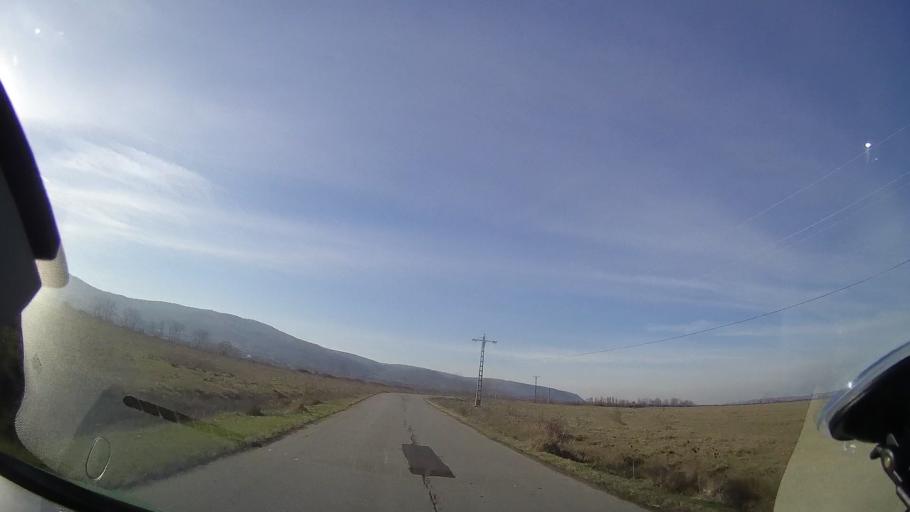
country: RO
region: Bihor
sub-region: Comuna Magesti
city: Magesti
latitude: 47.0165
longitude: 22.4641
